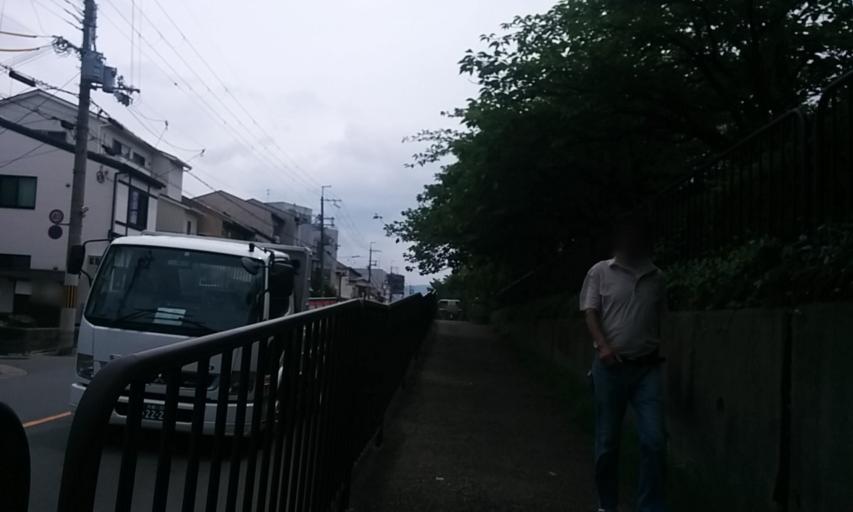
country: JP
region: Kyoto
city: Muko
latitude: 34.9841
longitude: 135.7365
